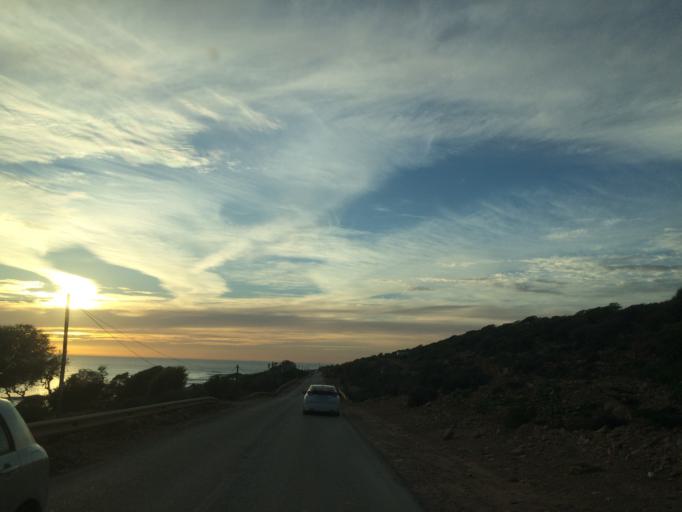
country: MA
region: Souss-Massa-Draa
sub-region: Agadir-Ida-ou-Tnan
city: Taghazout
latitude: 30.5473
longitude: -9.7179
